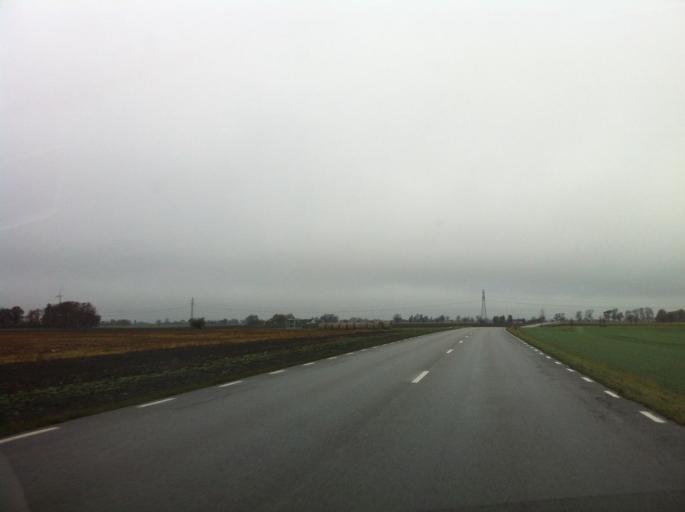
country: SE
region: Skane
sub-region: Lunds Kommun
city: Lund
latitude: 55.7503
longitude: 13.1646
